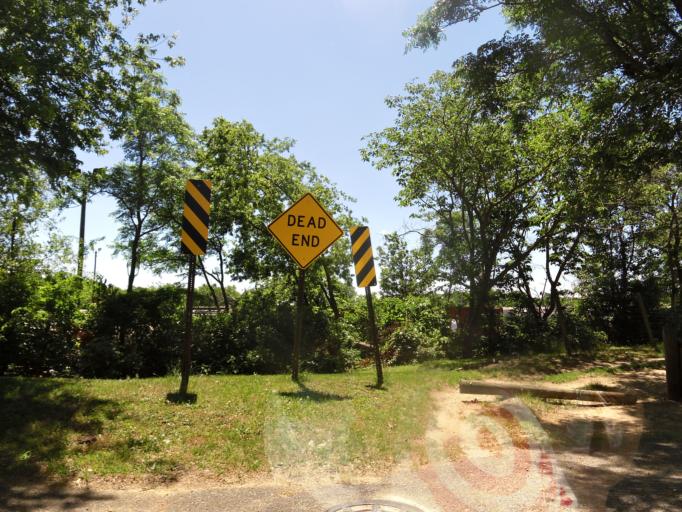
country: US
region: Georgia
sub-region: Richmond County
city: Augusta
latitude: 33.4555
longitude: -81.9779
